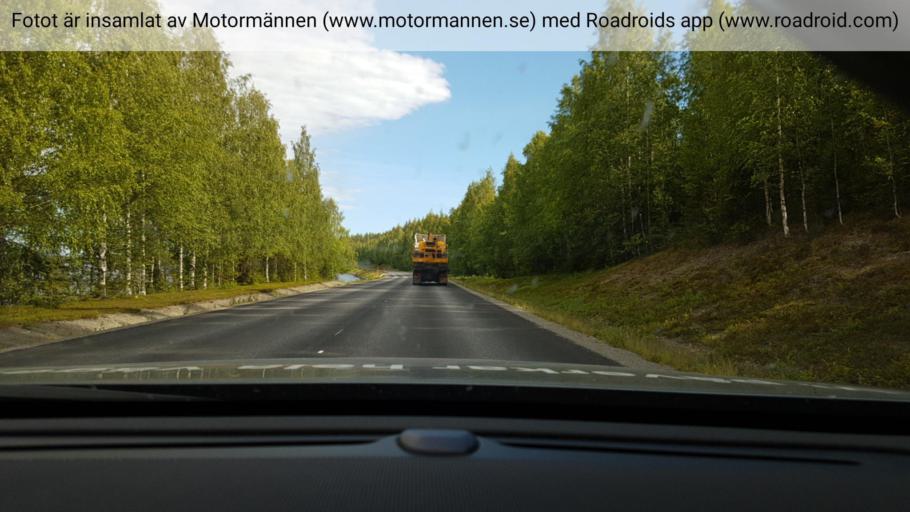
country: SE
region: Vaesterbotten
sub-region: Lycksele Kommun
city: Soderfors
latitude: 64.8455
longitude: 17.9679
